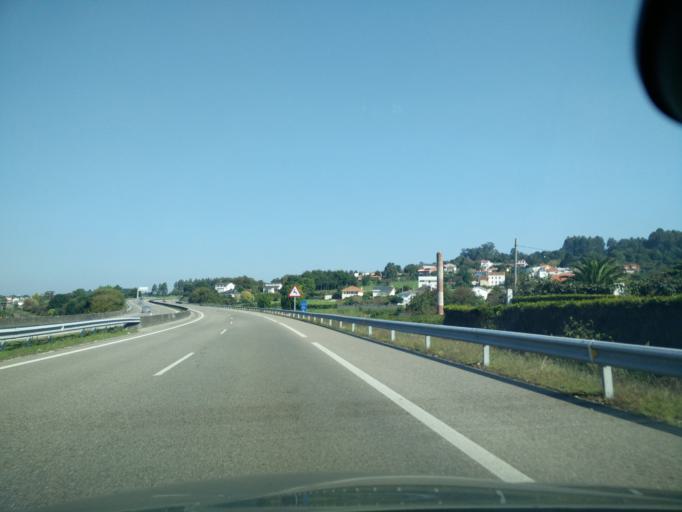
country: ES
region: Galicia
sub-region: Provincia da Coruna
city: Mino
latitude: 43.3572
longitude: -8.2022
